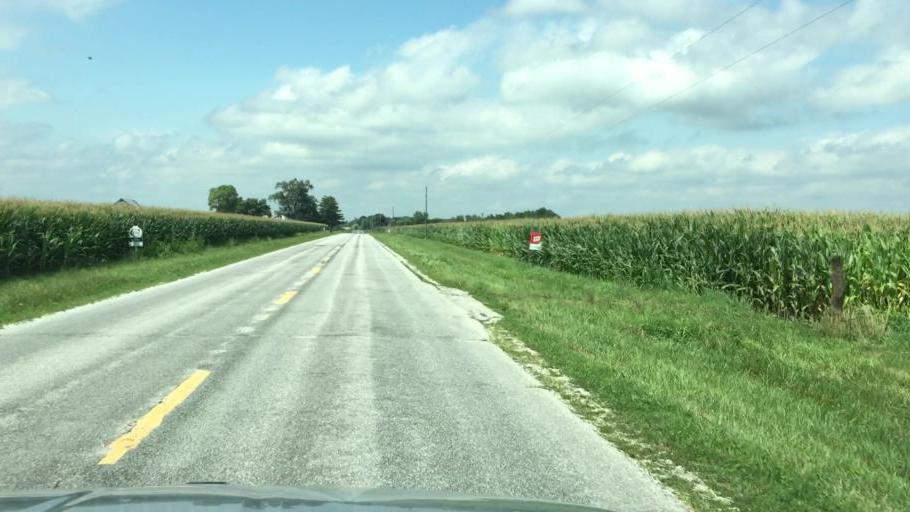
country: US
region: Illinois
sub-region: Hancock County
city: Nauvoo
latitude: 40.5145
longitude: -91.3081
